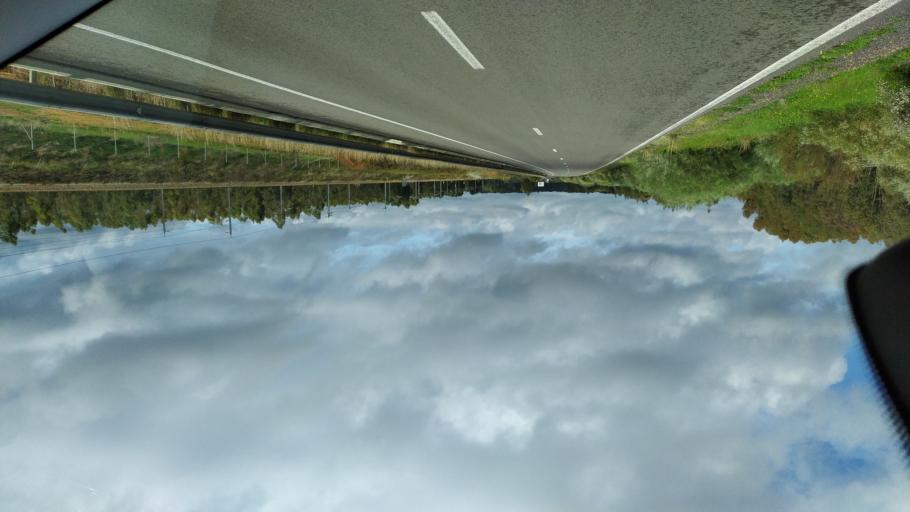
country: MA
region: Gharb-Chrarda-Beni Hssen
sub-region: Kenitra Province
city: Lalla Mimouna
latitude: 34.9042
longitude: -6.2080
